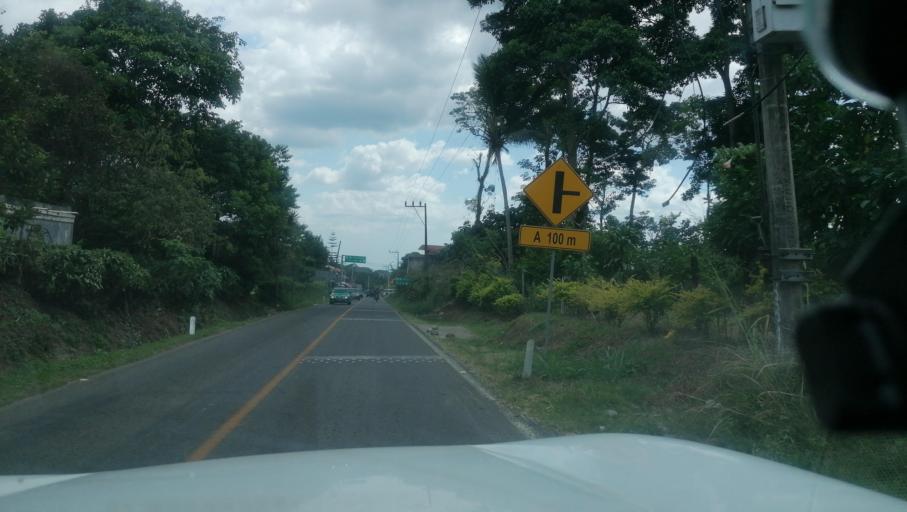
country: MX
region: Chiapas
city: Cacahoatan
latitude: 15.0327
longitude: -92.1536
